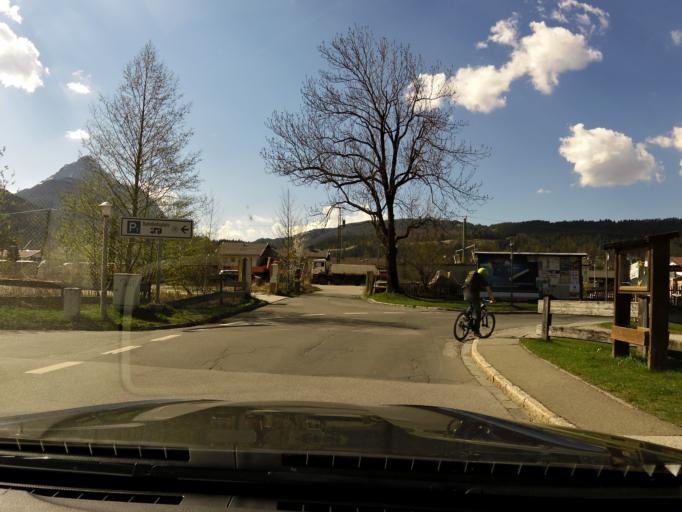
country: DE
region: Bavaria
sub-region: Upper Bavaria
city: Mittenwald
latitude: 47.4388
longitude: 11.2663
